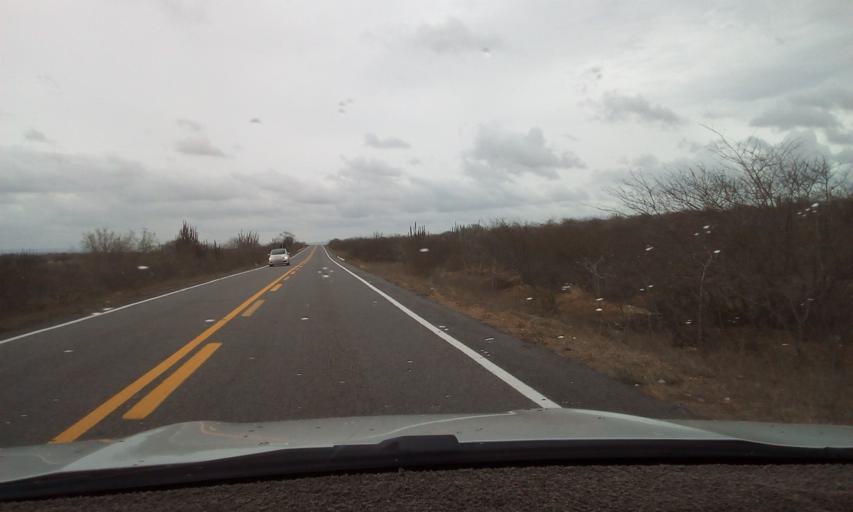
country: BR
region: Paraiba
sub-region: Areia
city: Remigio
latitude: -6.8840
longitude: -35.9221
